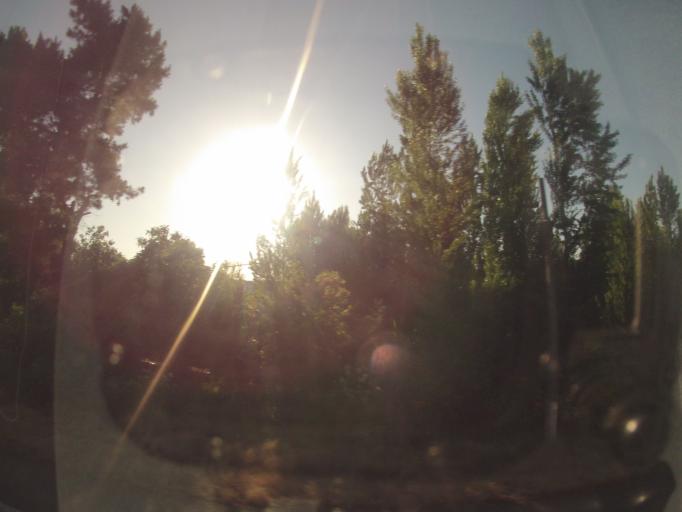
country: CL
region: O'Higgins
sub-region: Provincia de Colchagua
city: Chimbarongo
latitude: -34.7417
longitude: -71.0413
